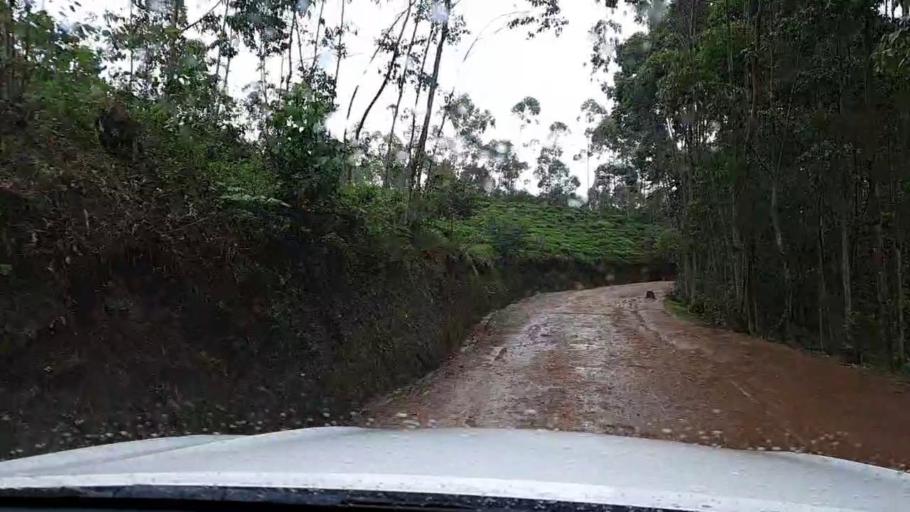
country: RW
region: Western Province
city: Cyangugu
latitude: -2.5477
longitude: 28.9791
